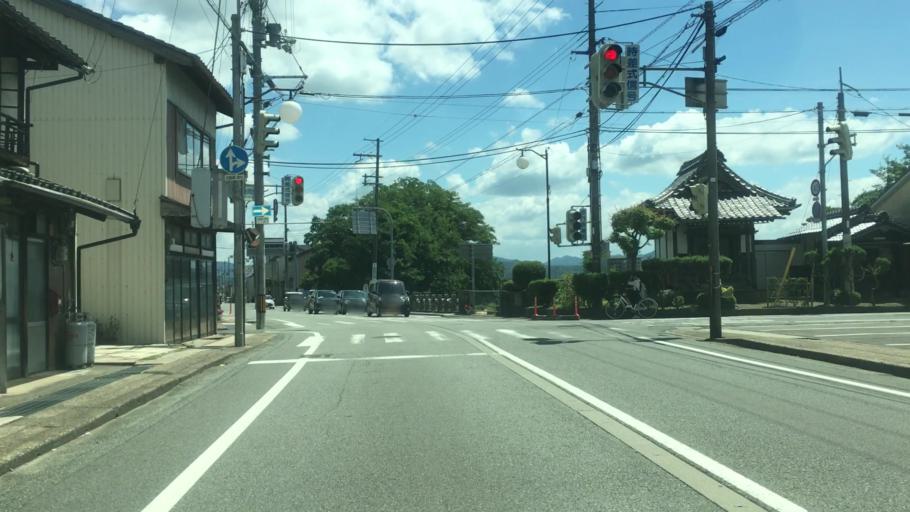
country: JP
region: Hyogo
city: Toyooka
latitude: 35.5357
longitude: 134.8254
